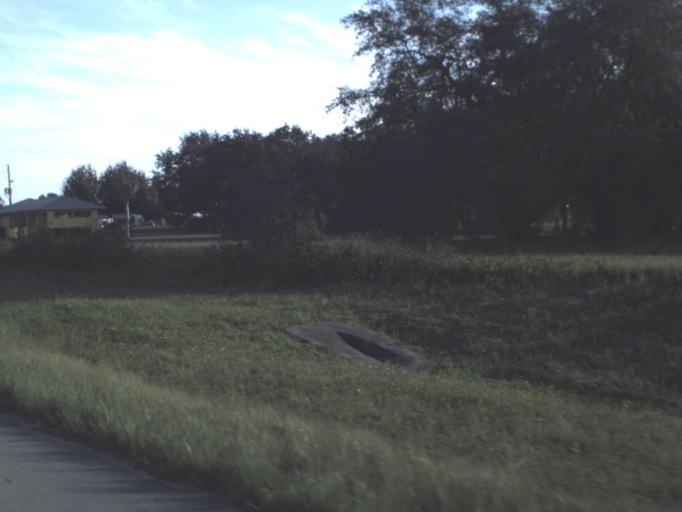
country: US
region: Florida
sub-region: Highlands County
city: Sebring
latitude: 27.4464
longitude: -81.4195
